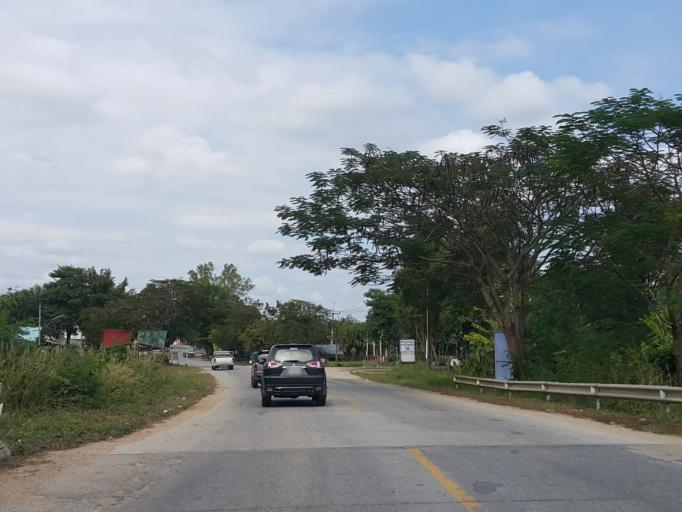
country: TH
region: Lampang
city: Lampang
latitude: 18.3643
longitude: 99.4582
